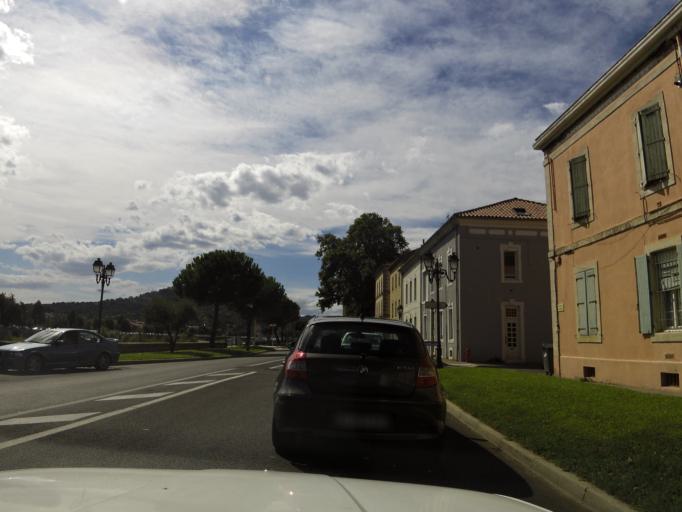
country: FR
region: Languedoc-Roussillon
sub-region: Departement du Gard
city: Ales
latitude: 44.1215
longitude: 4.0903
